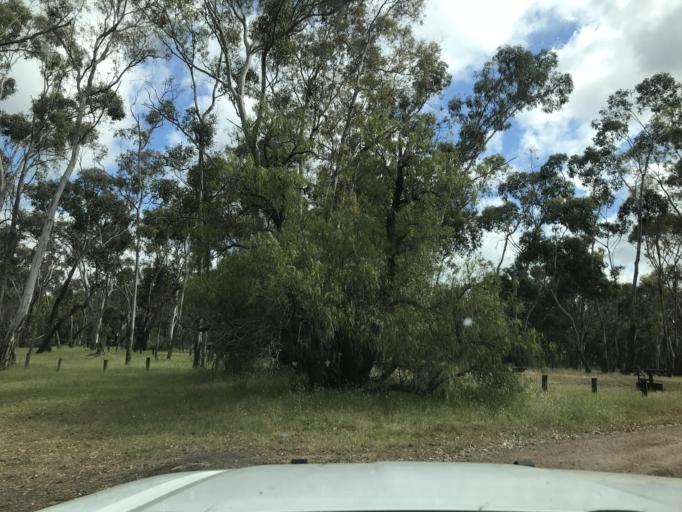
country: AU
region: South Australia
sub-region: Wattle Range
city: Penola
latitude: -37.2884
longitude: 141.1772
